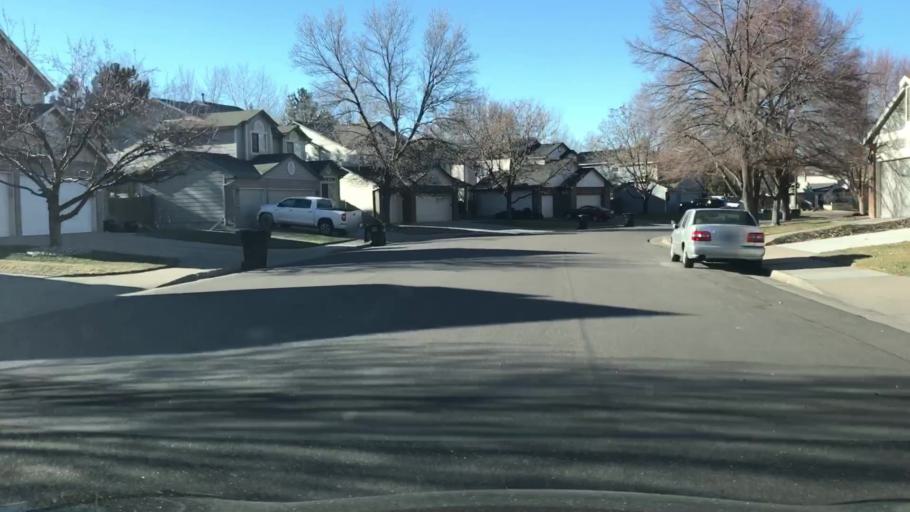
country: US
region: Colorado
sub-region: Arapahoe County
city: Glendale
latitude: 39.6871
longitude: -104.8957
